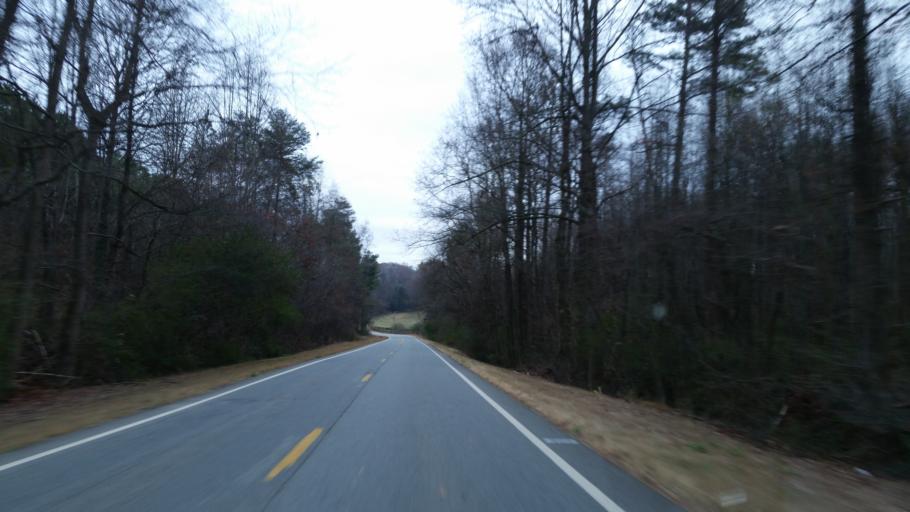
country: US
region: Georgia
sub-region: Dawson County
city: Dawsonville
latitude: 34.4751
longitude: -84.1558
